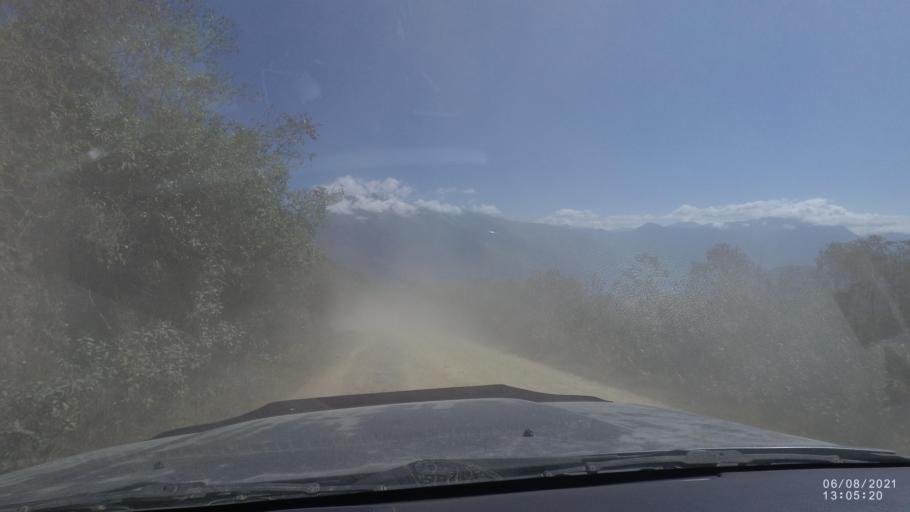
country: BO
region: La Paz
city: Quime
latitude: -16.7344
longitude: -66.7018
